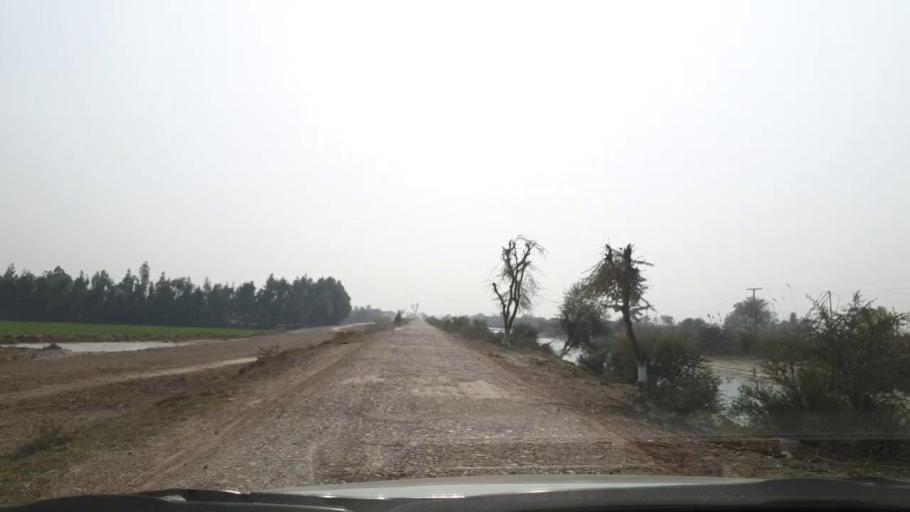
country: PK
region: Sindh
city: Matiari
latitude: 25.6421
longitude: 68.5604
